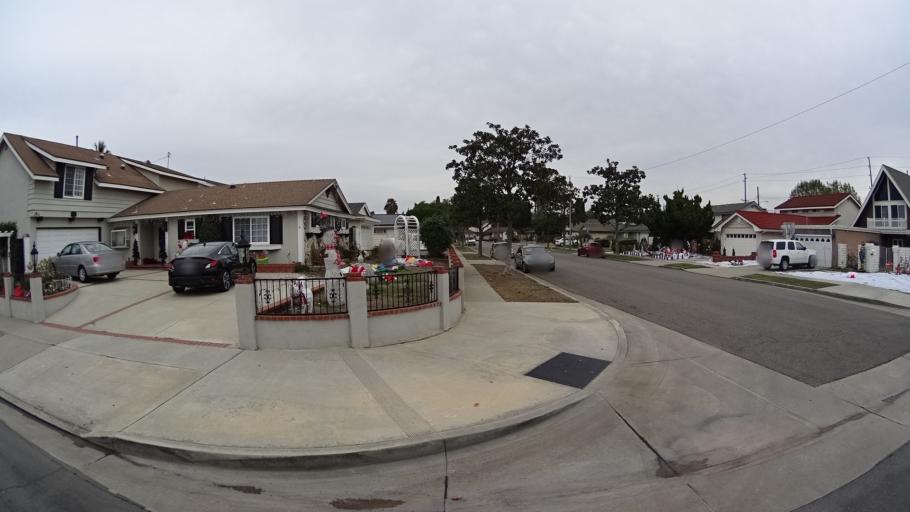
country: US
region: California
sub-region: Orange County
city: Tustin
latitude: 33.7427
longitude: -117.8073
